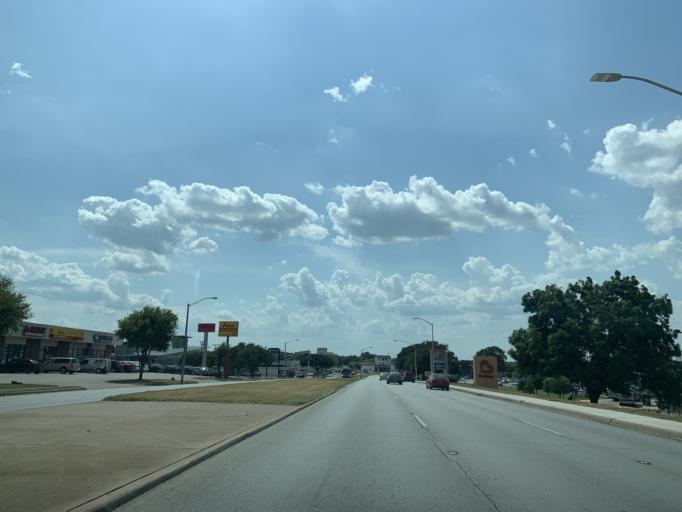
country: US
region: Texas
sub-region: Tarrant County
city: Edgecliff Village
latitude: 32.6845
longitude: -97.3232
